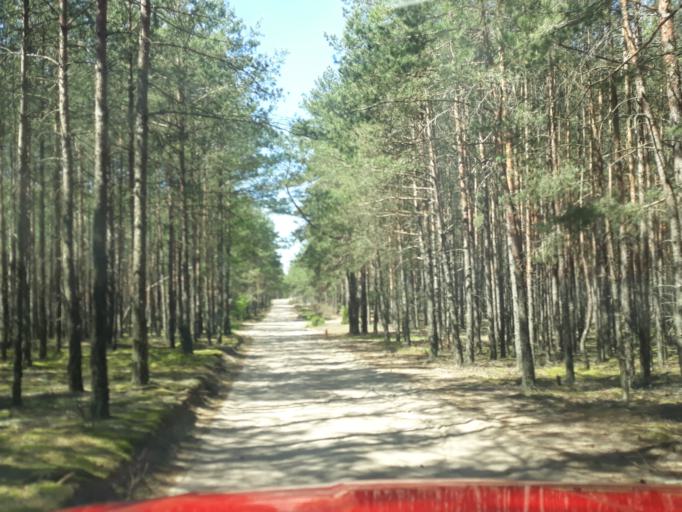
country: PL
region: Pomeranian Voivodeship
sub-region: Powiat chojnicki
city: Chojnice
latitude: 53.8667
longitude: 17.5363
